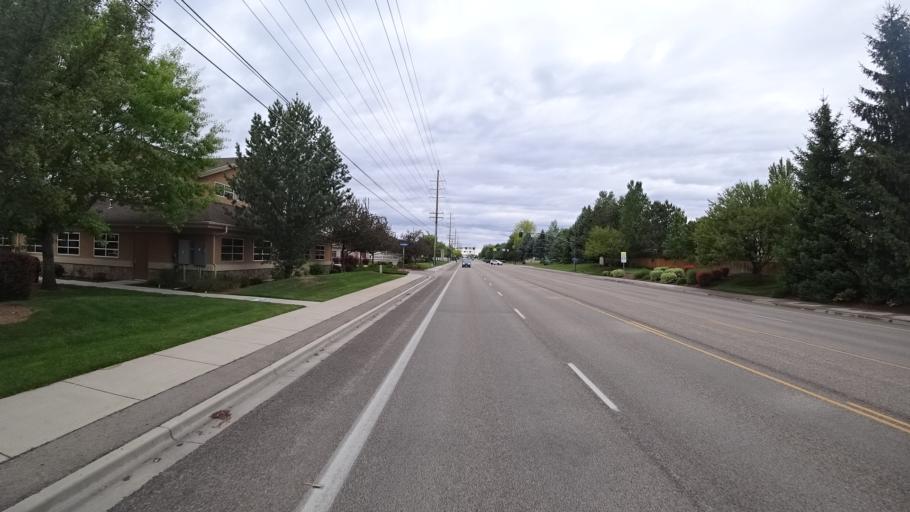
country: US
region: Idaho
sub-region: Ada County
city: Eagle
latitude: 43.6483
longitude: -116.3455
